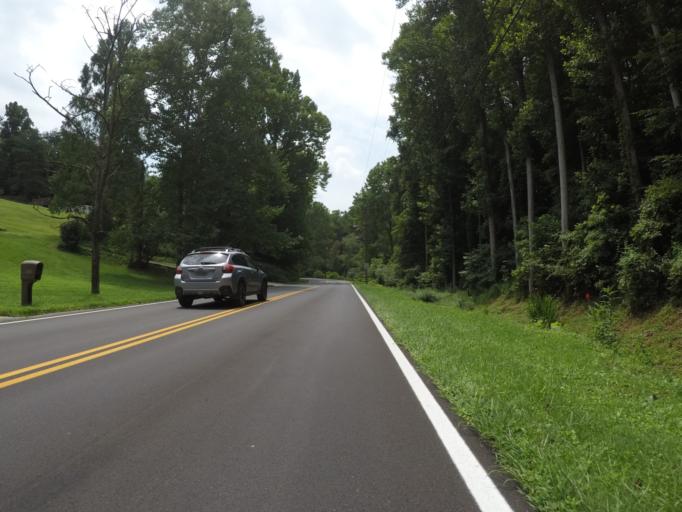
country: US
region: Kentucky
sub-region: Boyd County
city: Ashland
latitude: 38.4450
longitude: -82.6369
